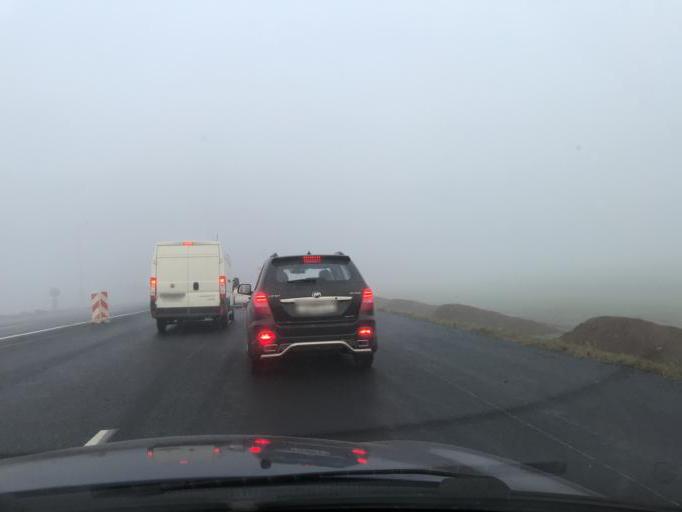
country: BY
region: Minsk
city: Valozhyn
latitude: 54.0640
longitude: 26.5262
